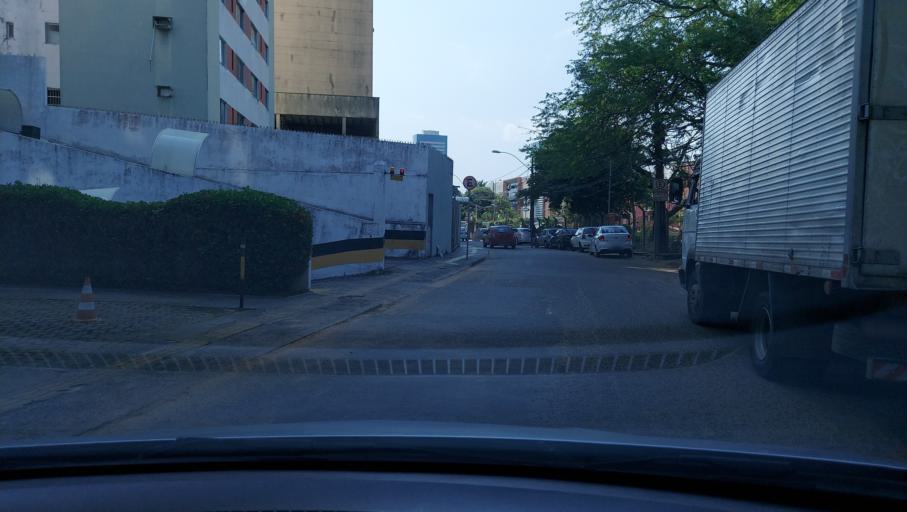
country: BR
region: Bahia
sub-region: Salvador
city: Salvador
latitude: -12.9818
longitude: -38.4527
